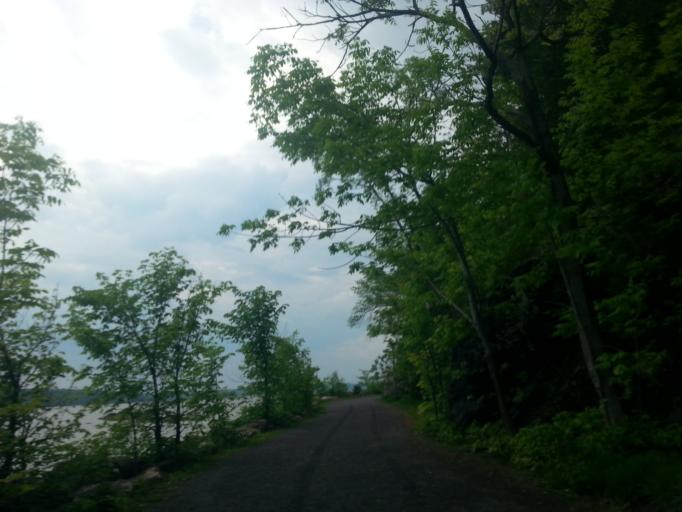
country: CA
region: Quebec
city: L'Ancienne-Lorette
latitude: 46.7500
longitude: -71.3169
